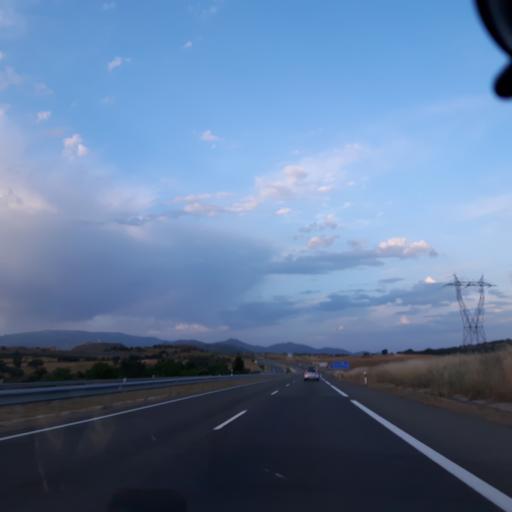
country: ES
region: Castille and Leon
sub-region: Provincia de Salamanca
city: Guijuelo
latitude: 40.5322
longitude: -5.6673
